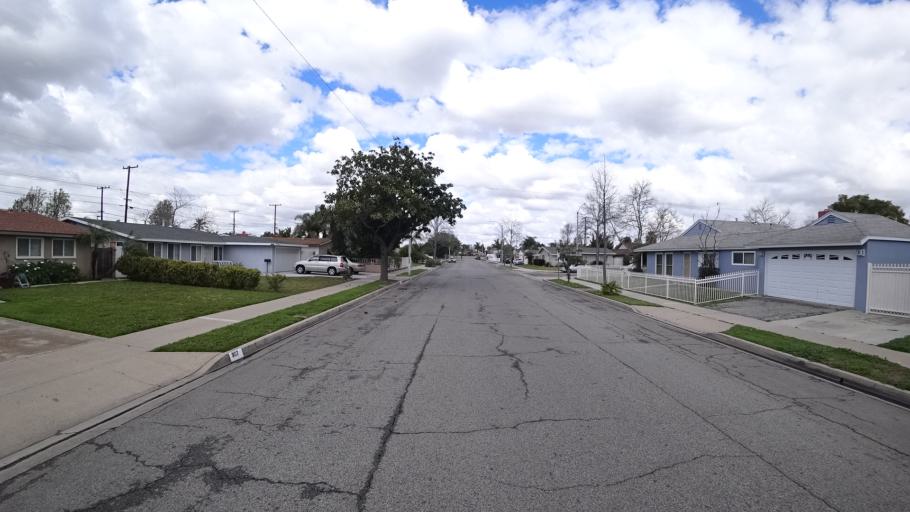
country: US
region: California
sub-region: Orange County
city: Anaheim
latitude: 33.8199
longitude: -117.9323
